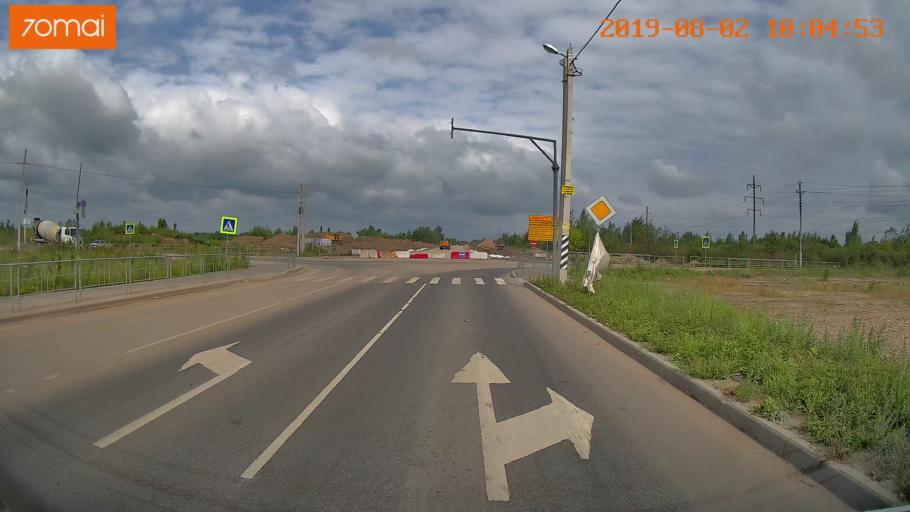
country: RU
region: Ivanovo
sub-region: Gorod Ivanovo
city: Ivanovo
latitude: 56.9760
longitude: 40.9220
